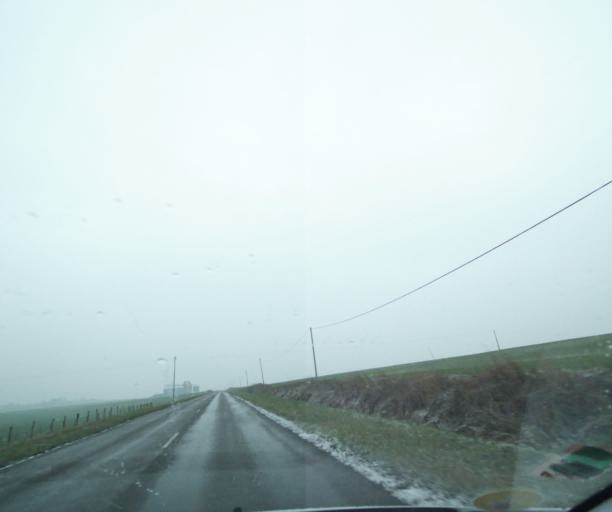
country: FR
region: Champagne-Ardenne
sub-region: Departement de la Haute-Marne
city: Wassy
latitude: 48.4875
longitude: 4.9776
